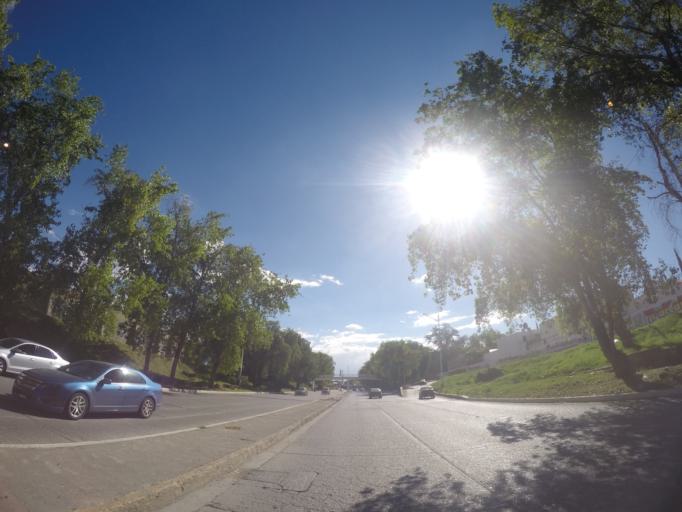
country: MX
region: San Luis Potosi
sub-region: San Luis Potosi
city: San Luis Potosi
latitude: 22.1696
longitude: -100.9776
